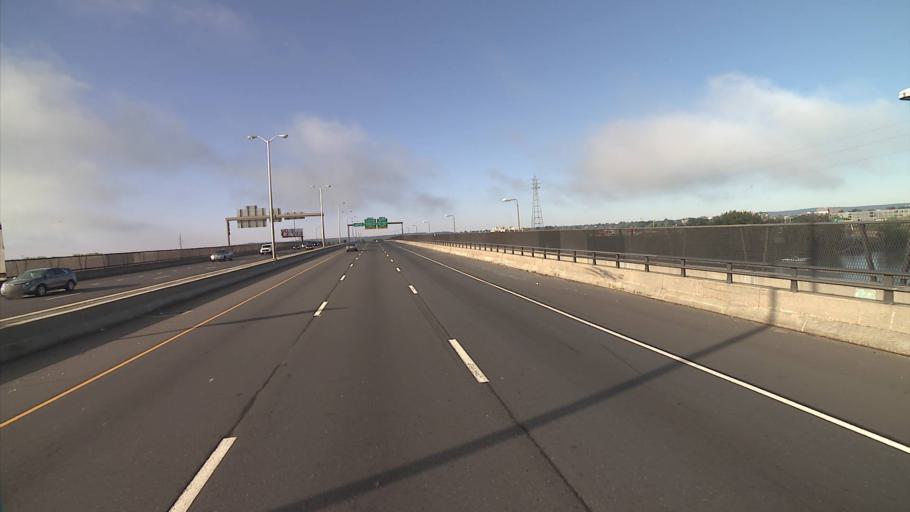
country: US
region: Connecticut
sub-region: Hartford County
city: Hartford
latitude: 41.7538
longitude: -72.6532
